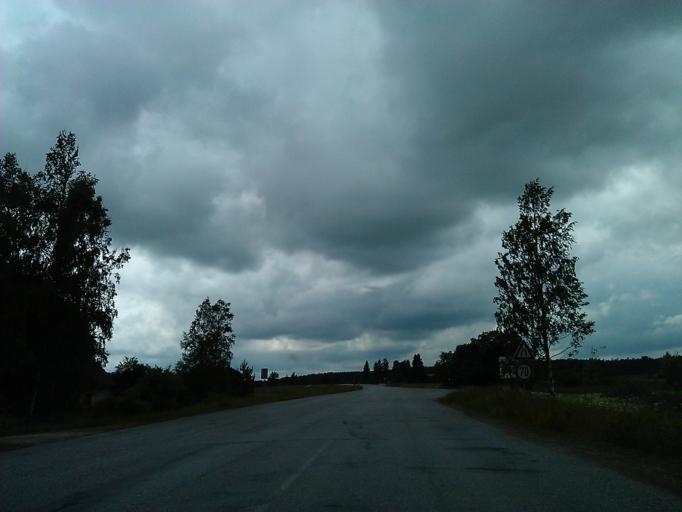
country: LV
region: Aizpute
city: Aizpute
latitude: 56.7950
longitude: 21.6638
